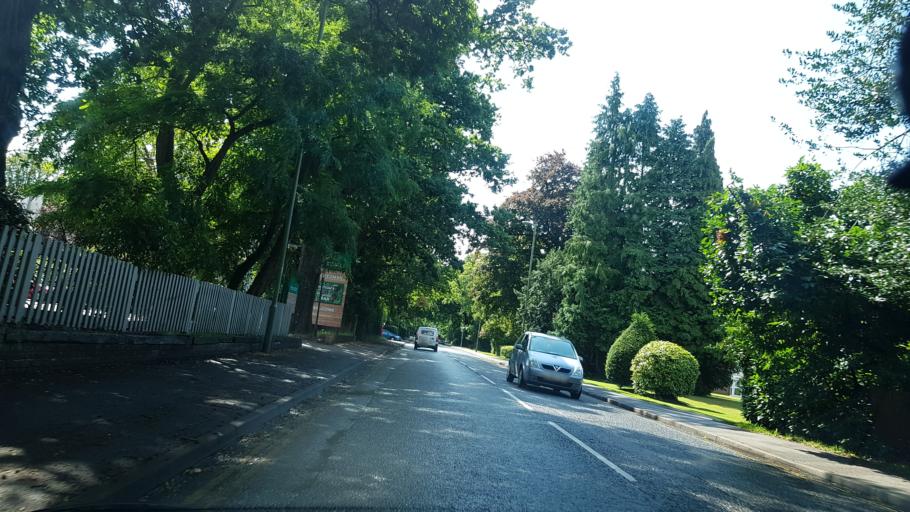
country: GB
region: England
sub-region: Surrey
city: West Byfleet
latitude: 51.3361
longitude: -0.5065
